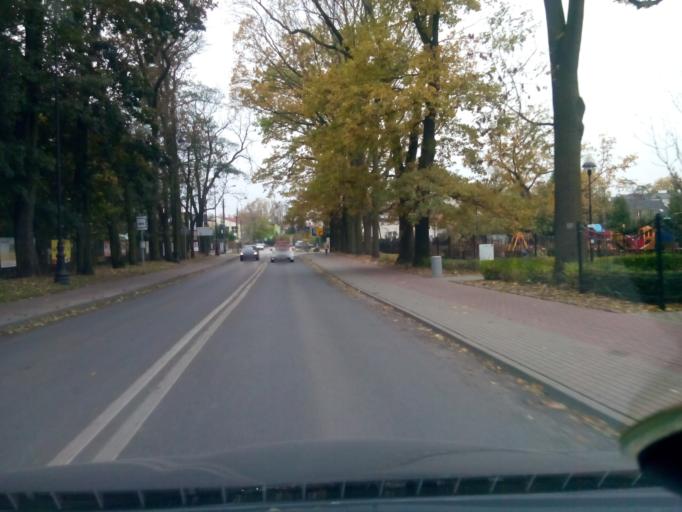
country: PL
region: Masovian Voivodeship
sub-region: Powiat grodziski
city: Grodzisk Mazowiecki
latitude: 52.1093
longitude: 20.6288
